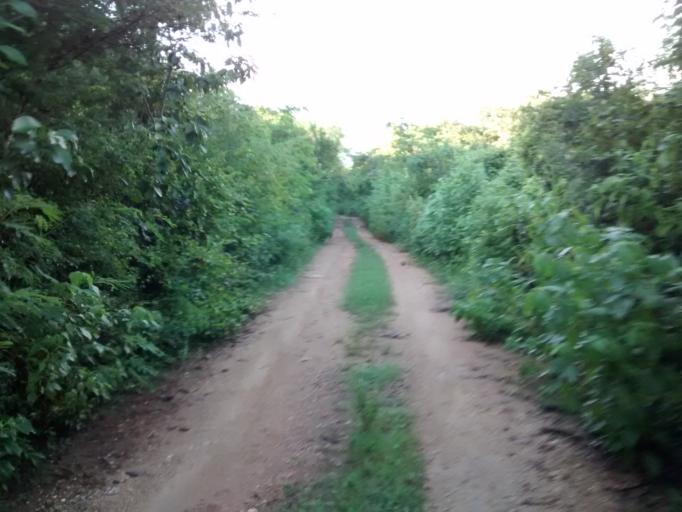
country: MX
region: Yucatan
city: Valladolid
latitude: 20.7173
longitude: -88.2061
